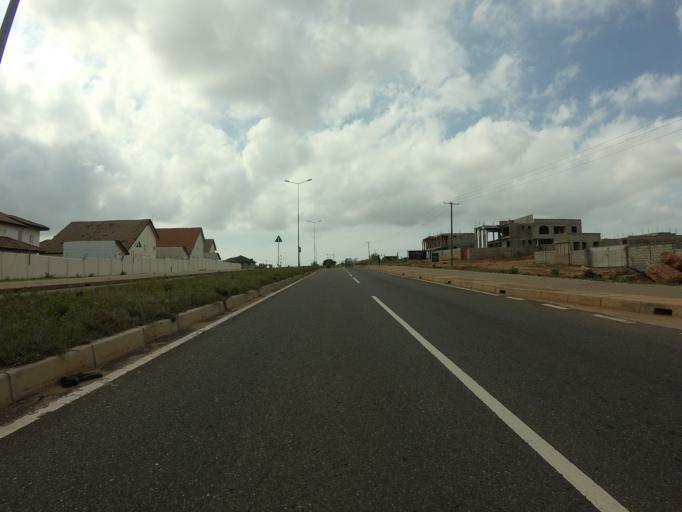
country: GH
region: Greater Accra
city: Teshi Old Town
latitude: 5.6077
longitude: -0.1402
